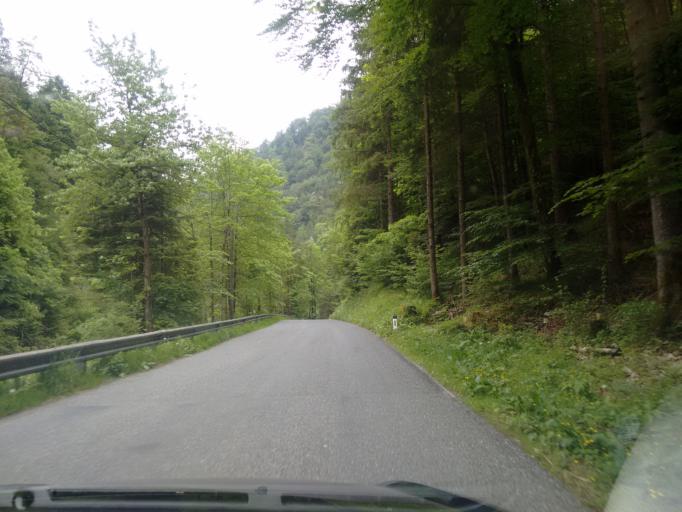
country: AT
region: Upper Austria
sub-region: Politischer Bezirk Gmunden
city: Ebensee
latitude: 47.8158
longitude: 13.7473
